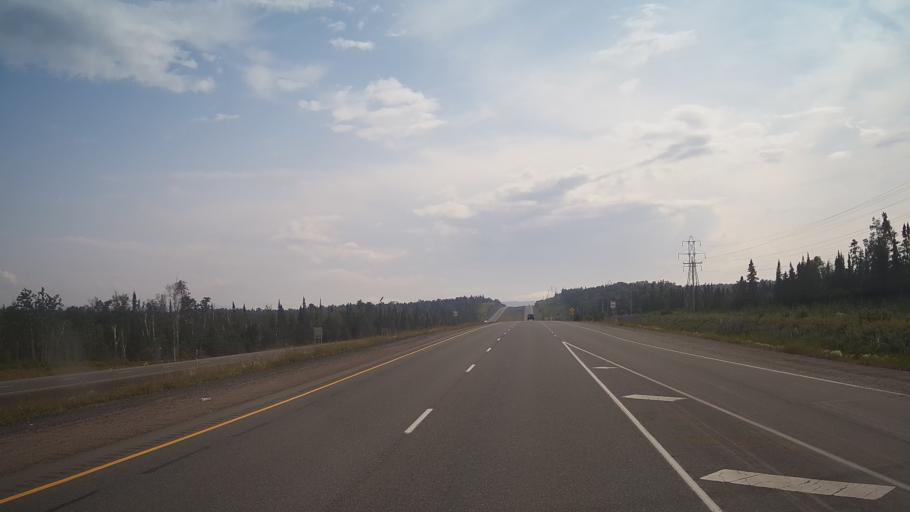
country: CA
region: Ontario
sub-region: Thunder Bay District
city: Thunder Bay
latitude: 48.6023
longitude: -88.7823
